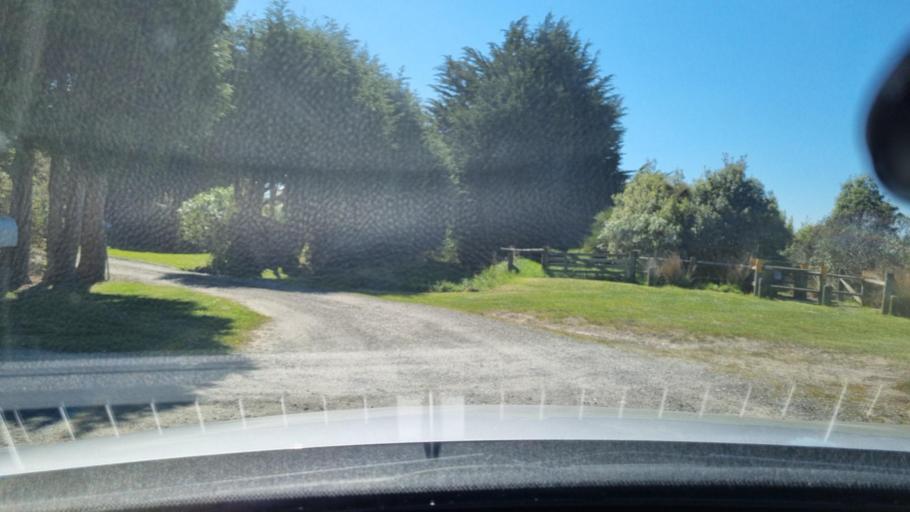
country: NZ
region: Southland
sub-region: Invercargill City
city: Invercargill
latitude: -46.4411
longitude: 168.3201
